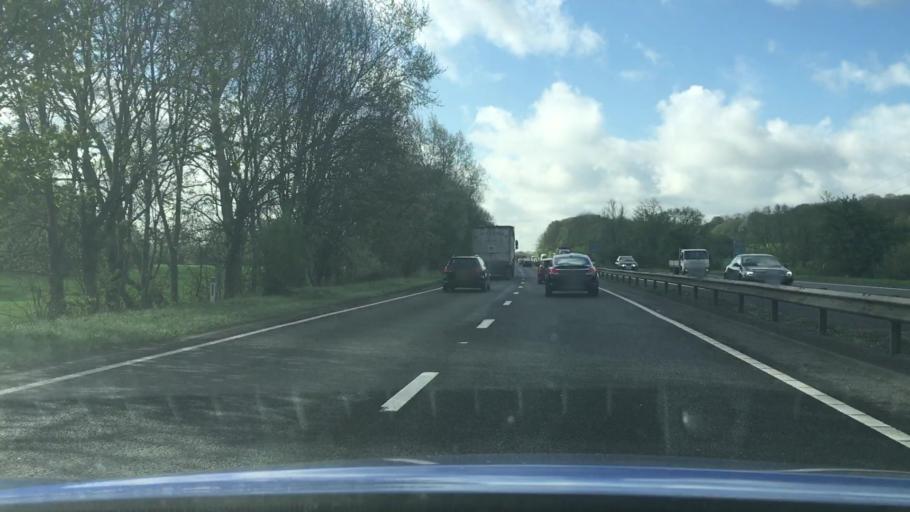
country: GB
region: England
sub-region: Oxfordshire
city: Yarnton
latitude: 51.7702
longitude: -1.3028
